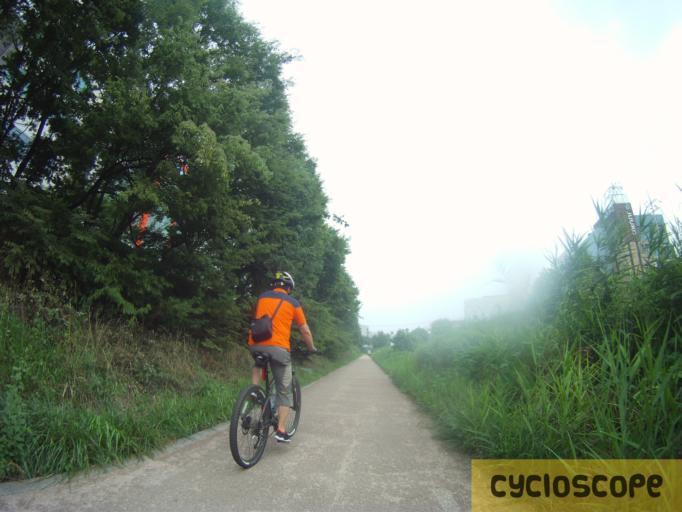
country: KR
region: Gyeonggi-do
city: Anyang-si
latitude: 37.3693
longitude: 126.9485
